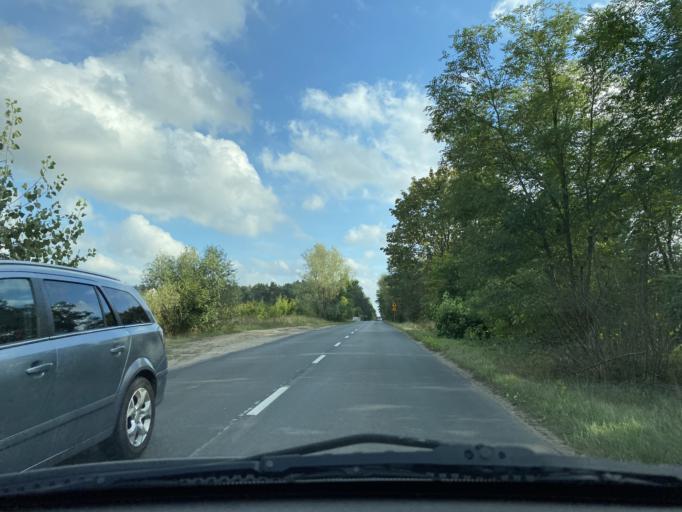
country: PL
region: Greater Poland Voivodeship
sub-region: Powiat poznanski
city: Dopiewo
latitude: 52.4142
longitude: 16.7183
